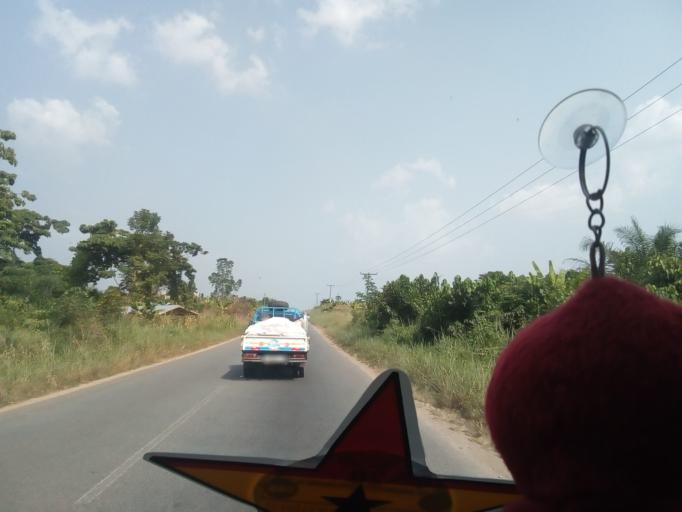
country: GH
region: Eastern
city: Suhum
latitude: 6.0444
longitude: -0.4209
